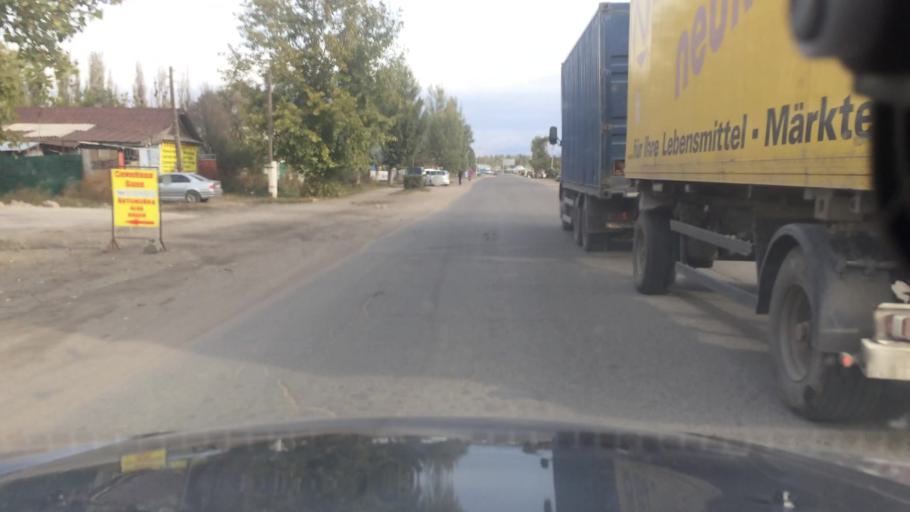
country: KG
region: Ysyk-Koel
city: Karakol
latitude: 42.5192
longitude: 78.3858
